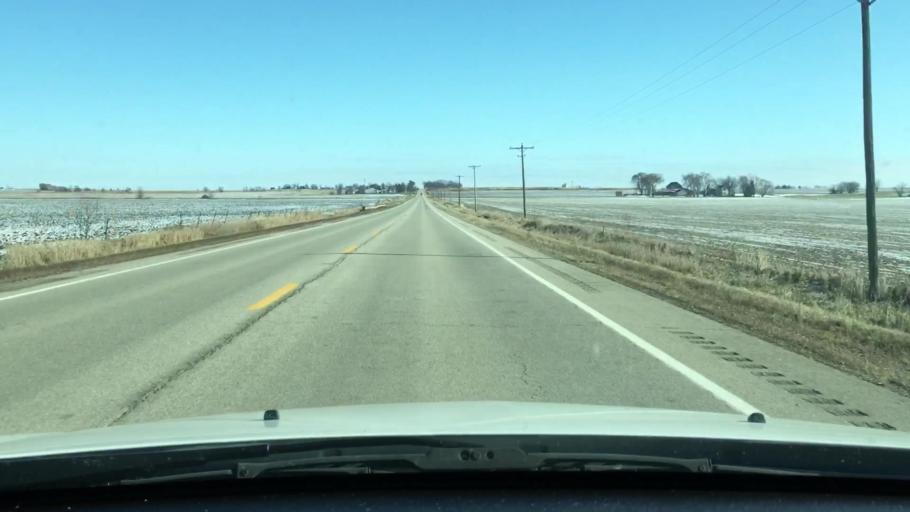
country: US
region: Illinois
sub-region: DeKalb County
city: Malta
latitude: 42.0008
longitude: -88.9257
